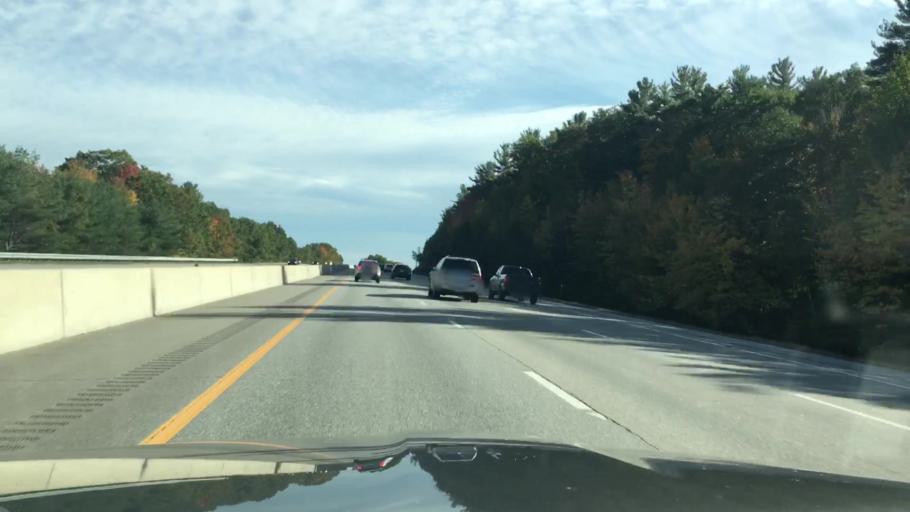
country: US
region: New Hampshire
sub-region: Merrimack County
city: Bow Bog
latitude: 43.1307
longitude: -71.4881
